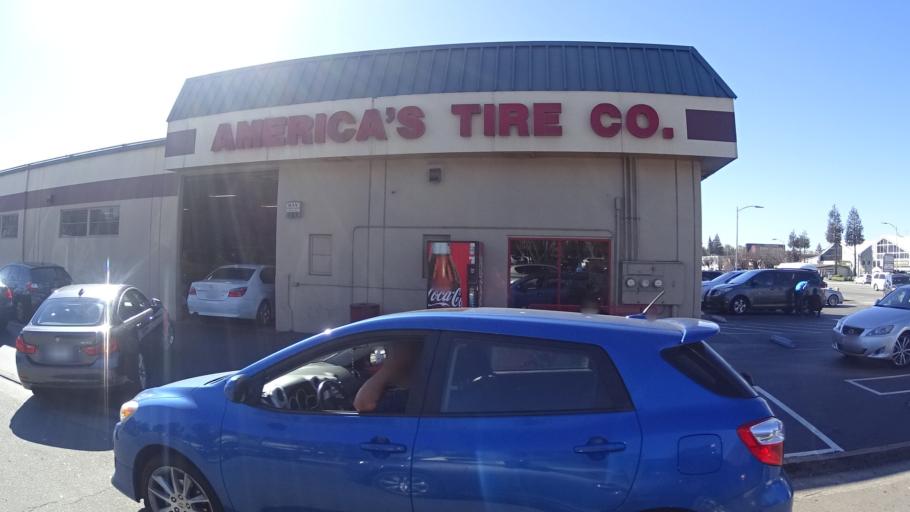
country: US
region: California
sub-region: Santa Clara County
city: San Jose
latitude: 37.3797
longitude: -121.9092
